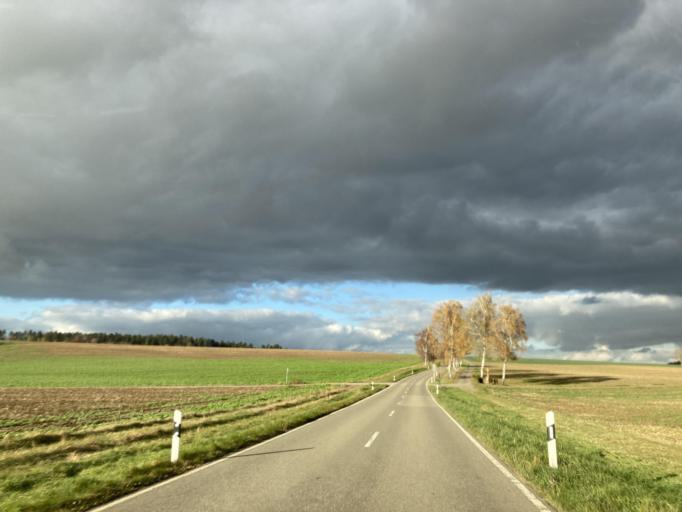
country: DE
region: Baden-Wuerttemberg
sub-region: Karlsruhe Region
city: Empfingen
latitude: 48.4023
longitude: 8.7509
